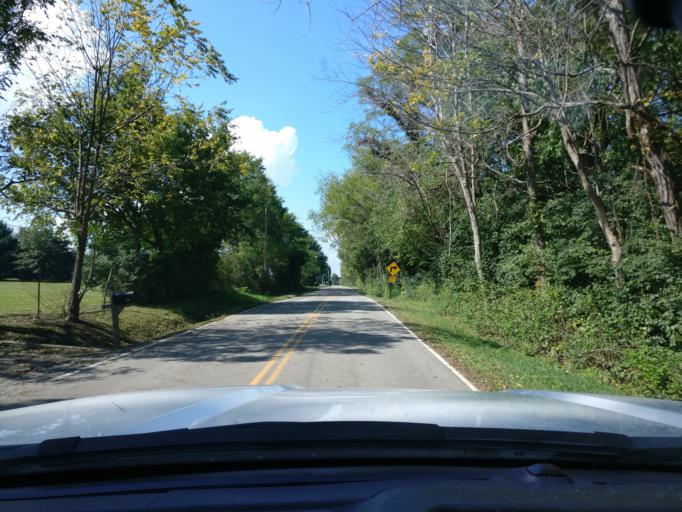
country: US
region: Ohio
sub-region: Warren County
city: Waynesville
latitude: 39.4859
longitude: -83.9935
